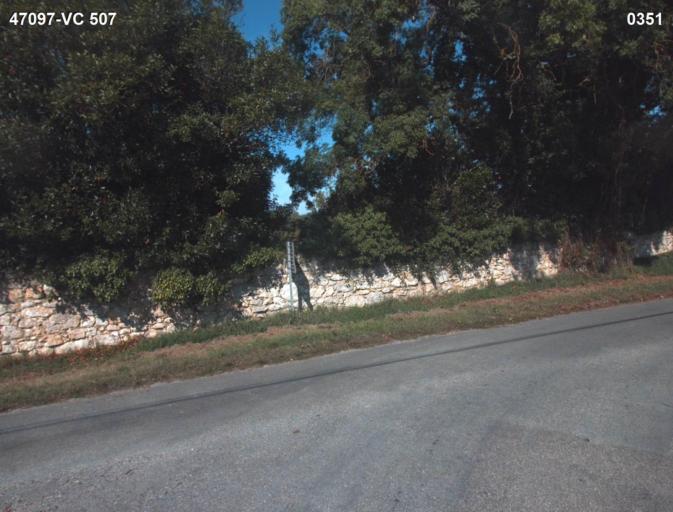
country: FR
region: Aquitaine
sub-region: Departement du Lot-et-Garonne
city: Port-Sainte-Marie
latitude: 44.2391
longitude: 0.3886
